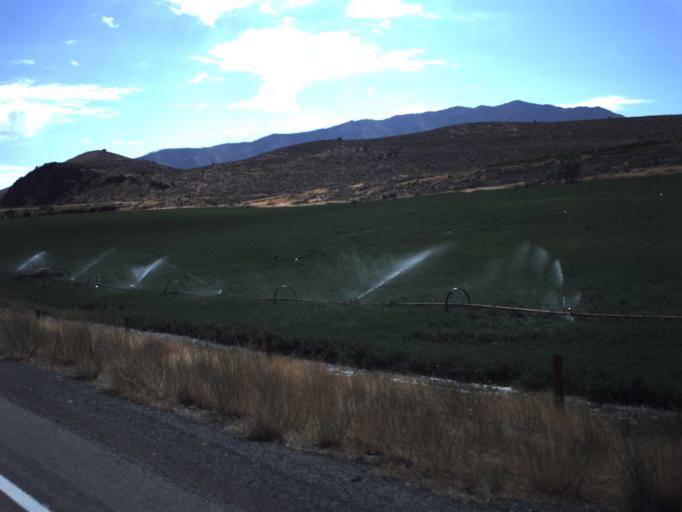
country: US
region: Utah
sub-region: Utah County
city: Genola
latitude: 39.9765
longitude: -111.8436
